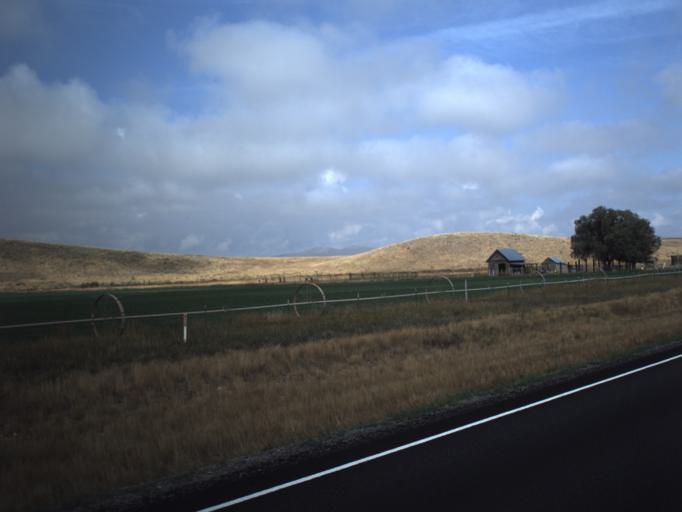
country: US
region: Utah
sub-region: Rich County
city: Randolph
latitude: 41.5309
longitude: -111.1629
